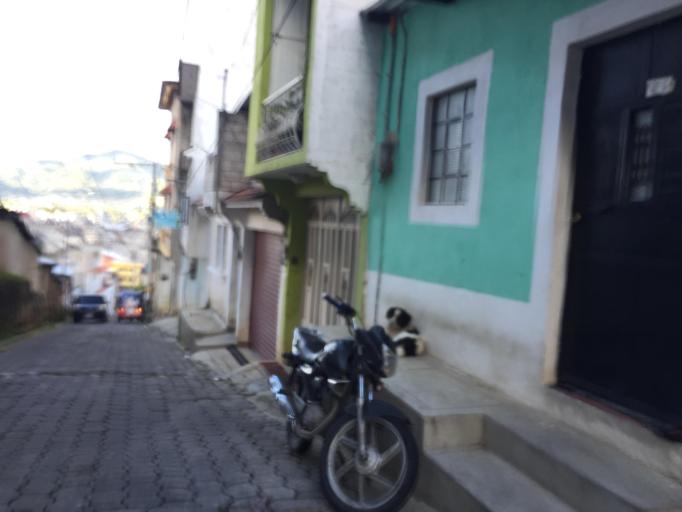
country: GT
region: Totonicapan
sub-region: Municipio de Totonicapan
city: Totonicapan
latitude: 14.9163
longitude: -91.3551
